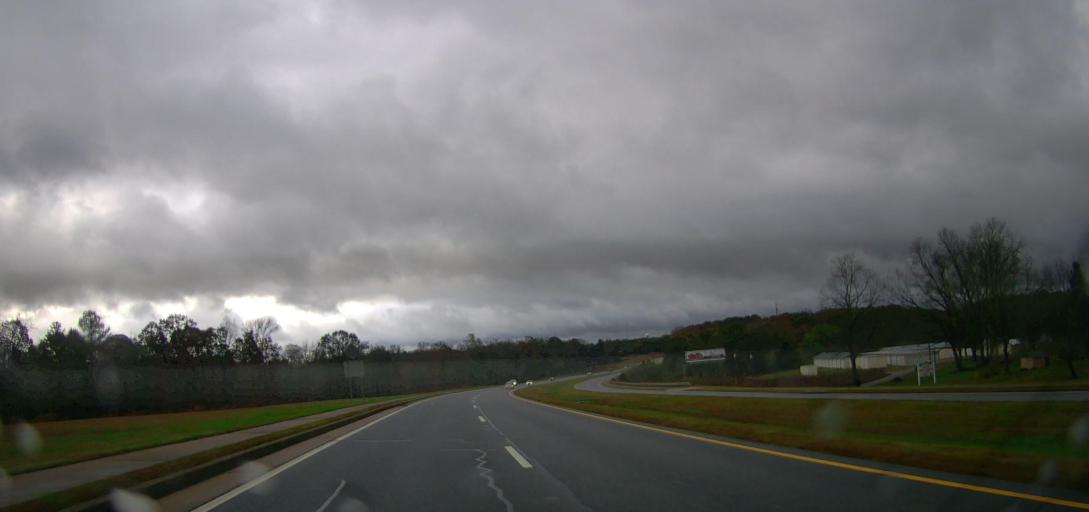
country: US
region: Georgia
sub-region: Jackson County
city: Nicholson
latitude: 34.1316
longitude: -83.4282
